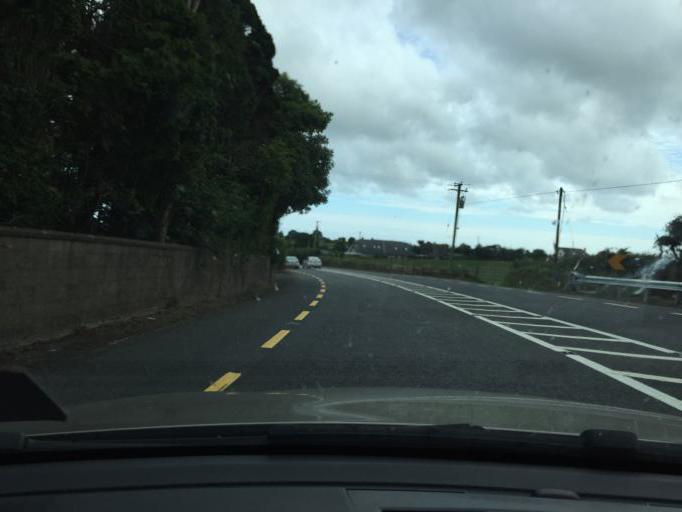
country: IE
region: Munster
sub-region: Waterford
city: Dungarvan
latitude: 52.1209
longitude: -7.5638
